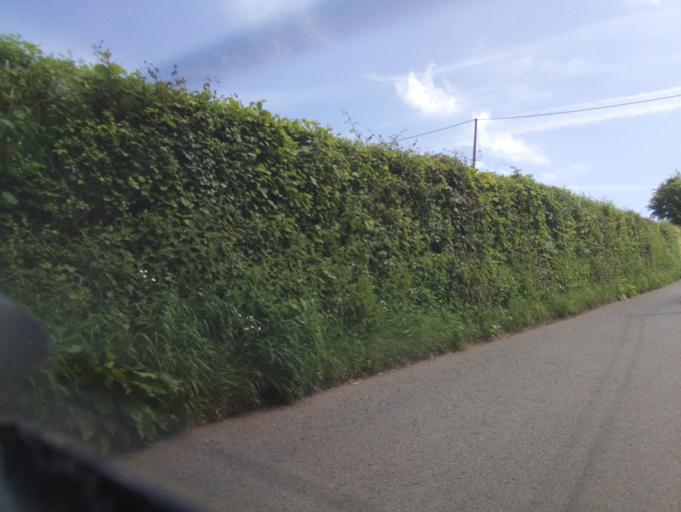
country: GB
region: England
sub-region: Herefordshire
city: Llanrothal
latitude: 51.8712
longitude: -2.8042
